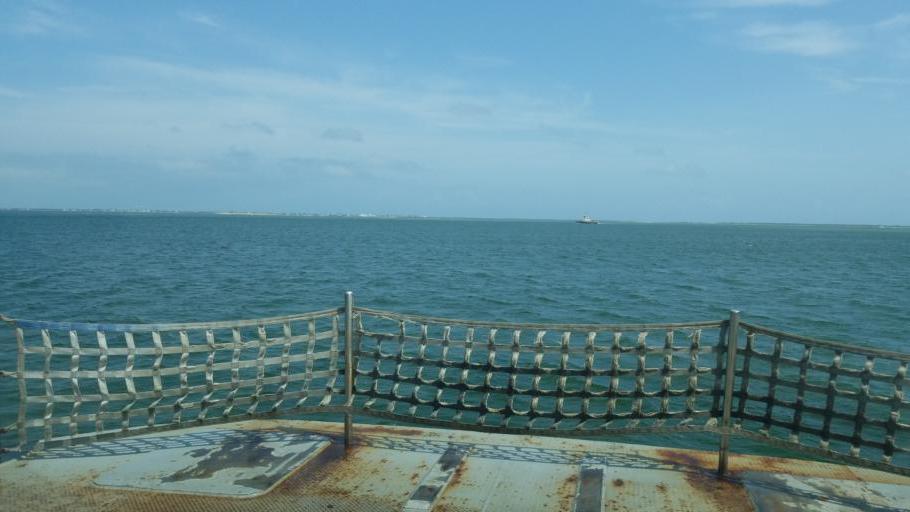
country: US
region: North Carolina
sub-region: Dare County
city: Buxton
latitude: 35.2186
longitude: -75.7396
